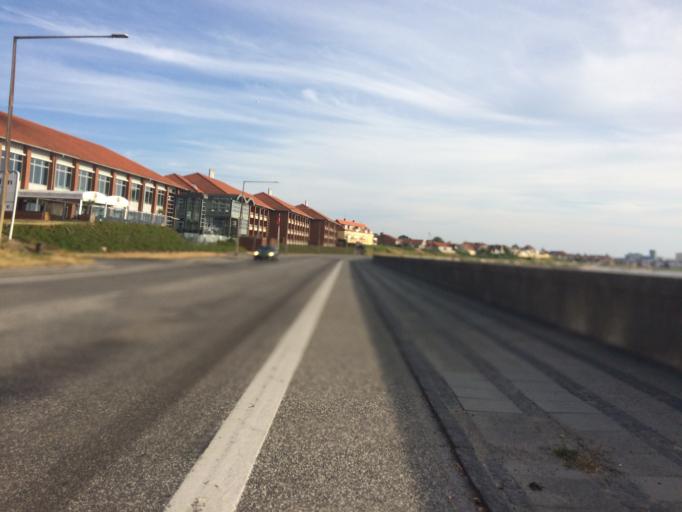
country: DK
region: Capital Region
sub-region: Bornholm Kommune
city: Ronne
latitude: 55.1085
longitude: 14.7004
